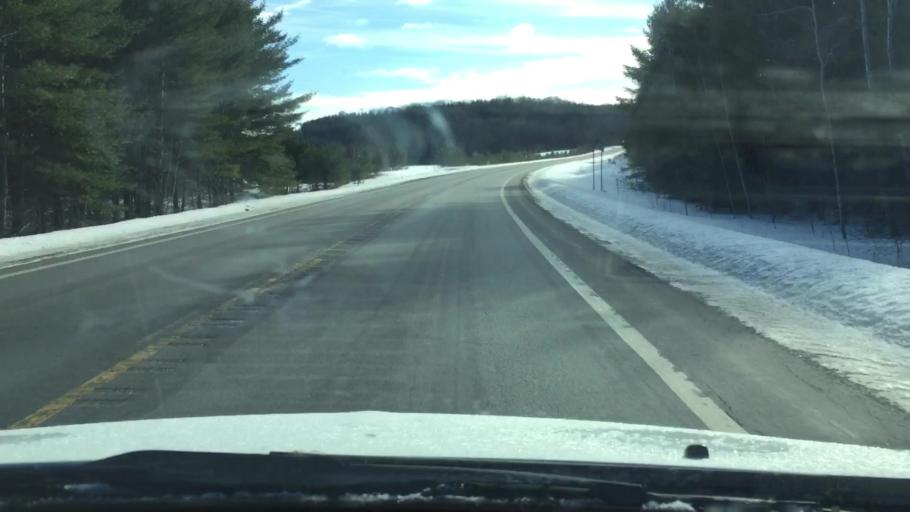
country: US
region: Michigan
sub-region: Antrim County
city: Mancelona
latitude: 44.9821
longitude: -85.0538
